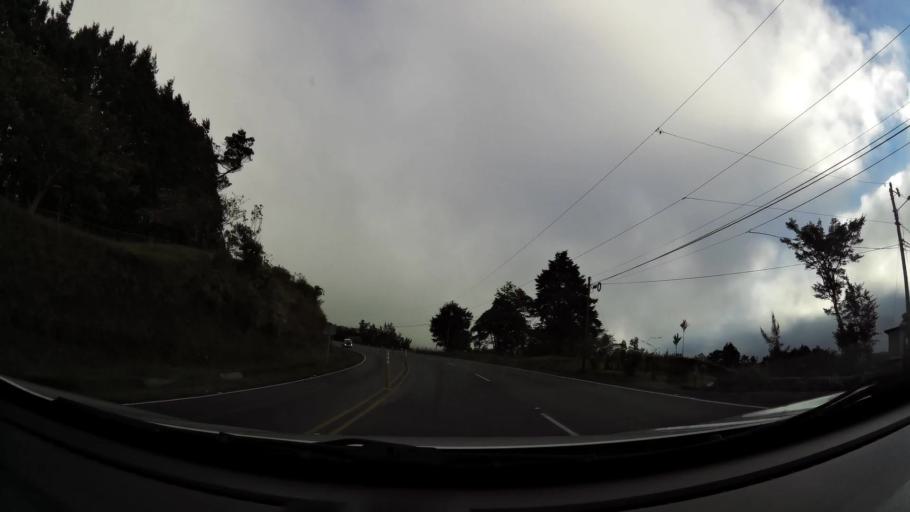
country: CR
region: Heredia
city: Angeles
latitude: 10.0319
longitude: -84.0031
